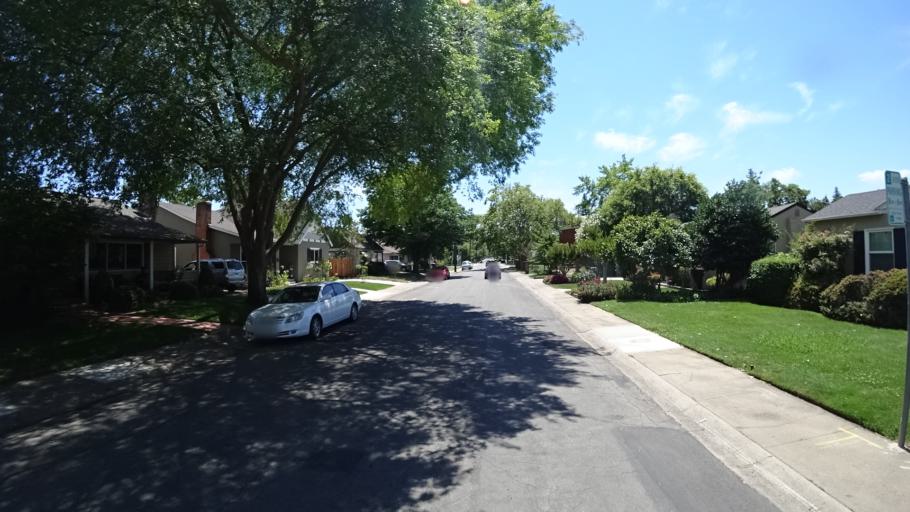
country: US
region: California
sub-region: Sacramento County
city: Sacramento
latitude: 38.5693
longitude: -121.4375
